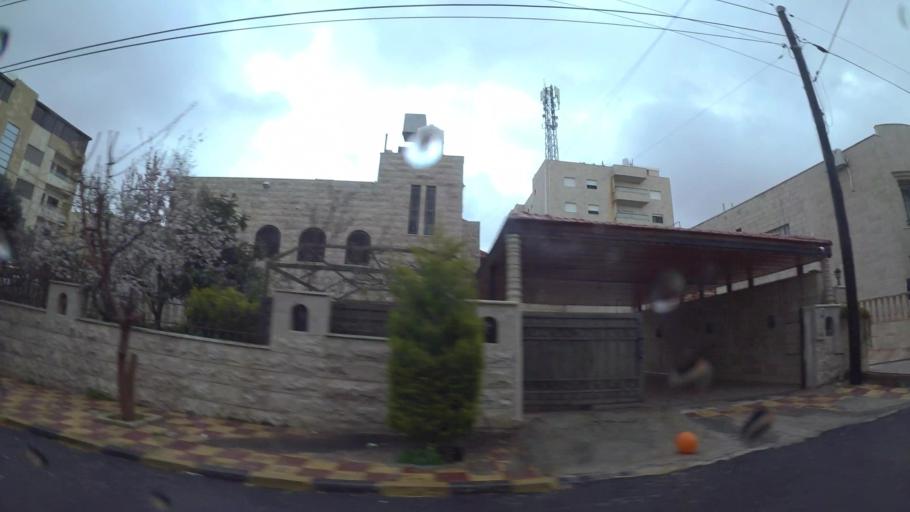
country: JO
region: Amman
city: Al Jubayhah
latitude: 32.0330
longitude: 35.8714
